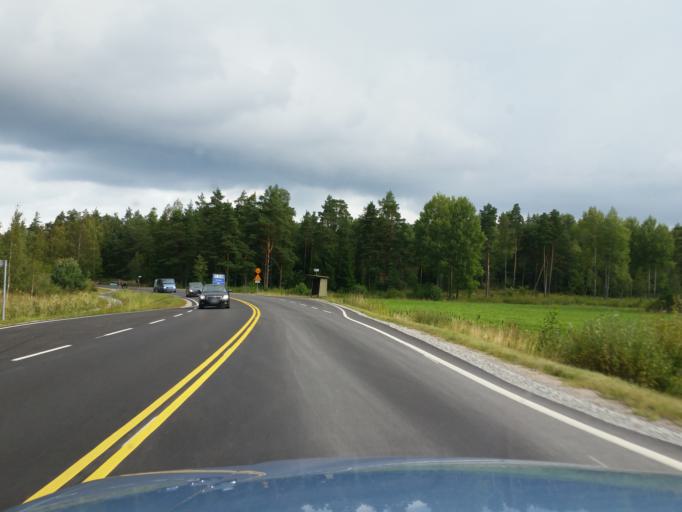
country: FI
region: Varsinais-Suomi
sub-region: Aboland-Turunmaa
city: Laensi-Turunmaa
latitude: 60.2488
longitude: 22.2423
